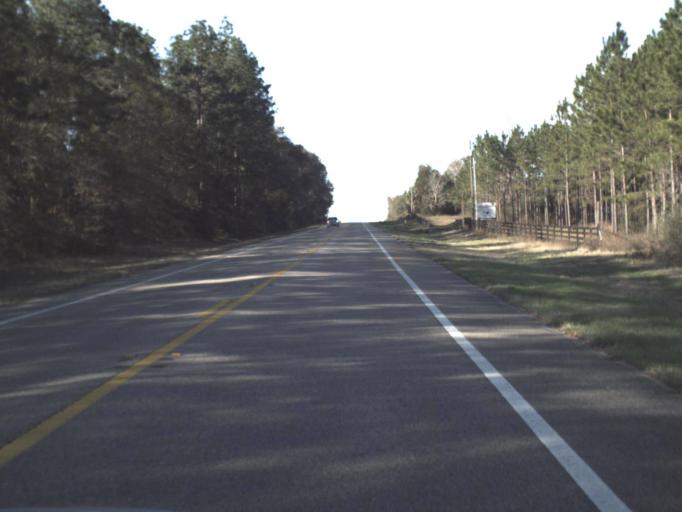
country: US
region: Florida
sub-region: Jackson County
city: Marianna
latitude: 30.6004
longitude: -85.1813
